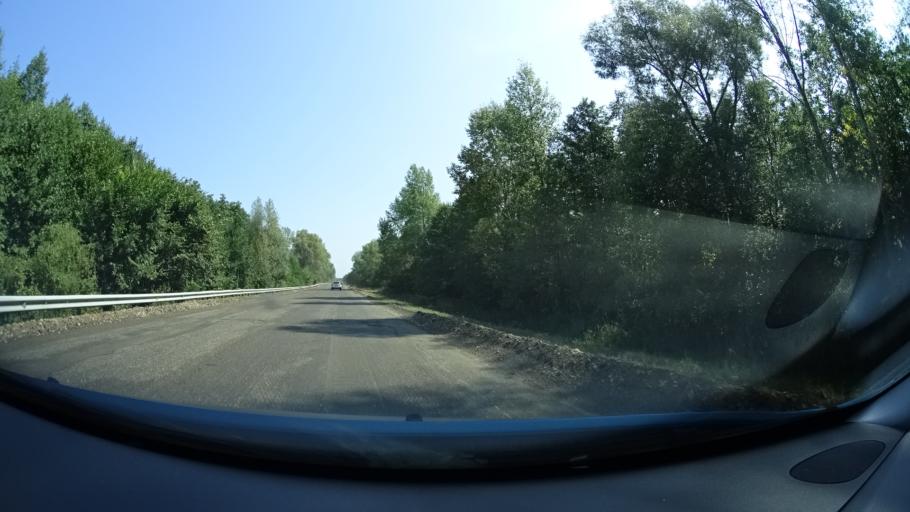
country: RU
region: Bashkortostan
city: Ulukulevo
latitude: 54.4543
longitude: 56.4952
